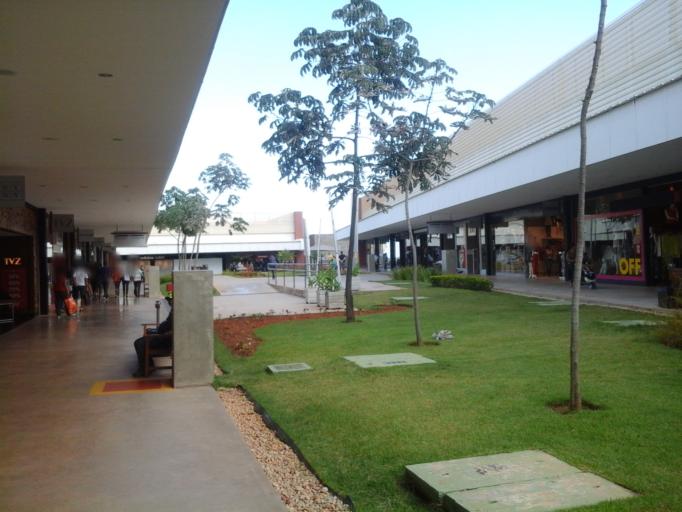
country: BR
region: Goias
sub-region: Abadiania
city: Abadiania
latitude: -16.1218
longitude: -48.3985
